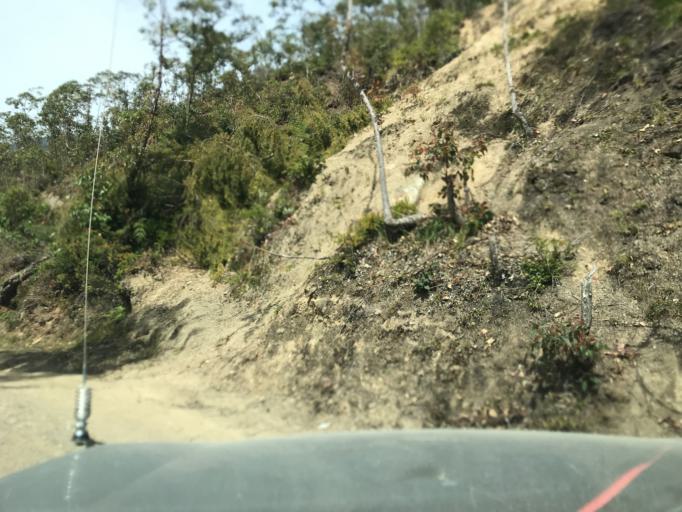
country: TL
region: Ainaro
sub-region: Ainaro
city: Ainaro
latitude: -8.8827
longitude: 125.5275
